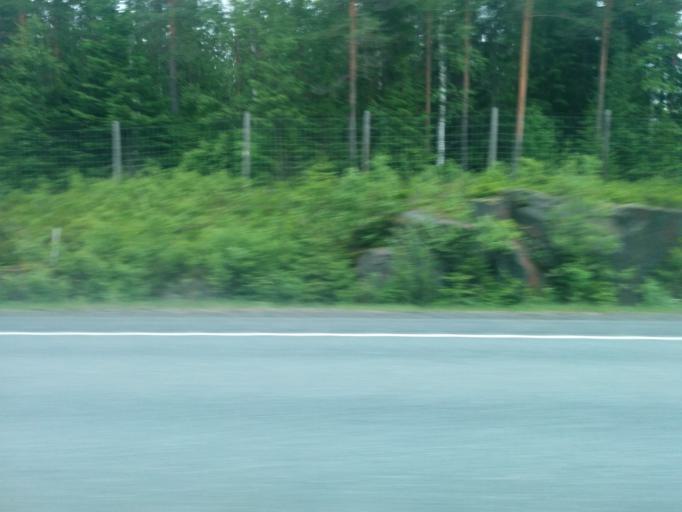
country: FI
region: Pirkanmaa
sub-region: Tampere
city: Orivesi
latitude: 61.6648
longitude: 24.2685
